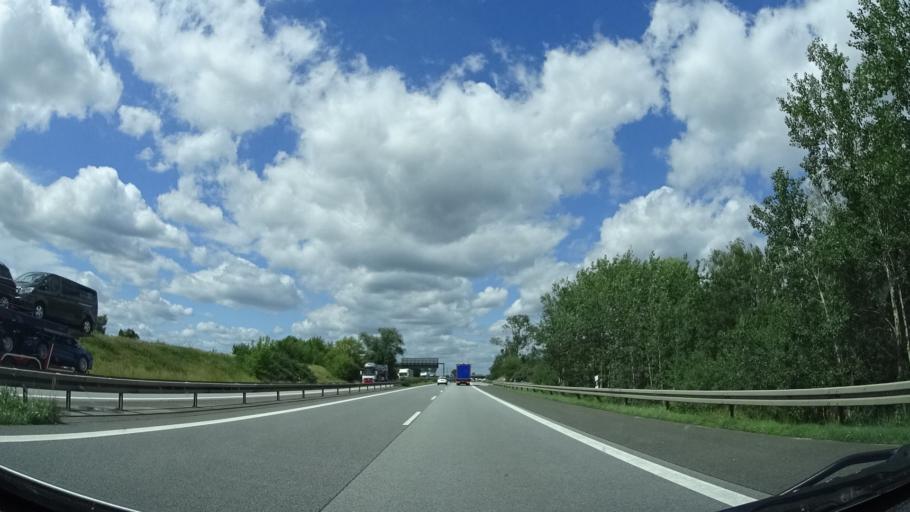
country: DE
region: Berlin
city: Blankenfelde
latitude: 52.6490
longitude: 13.4197
